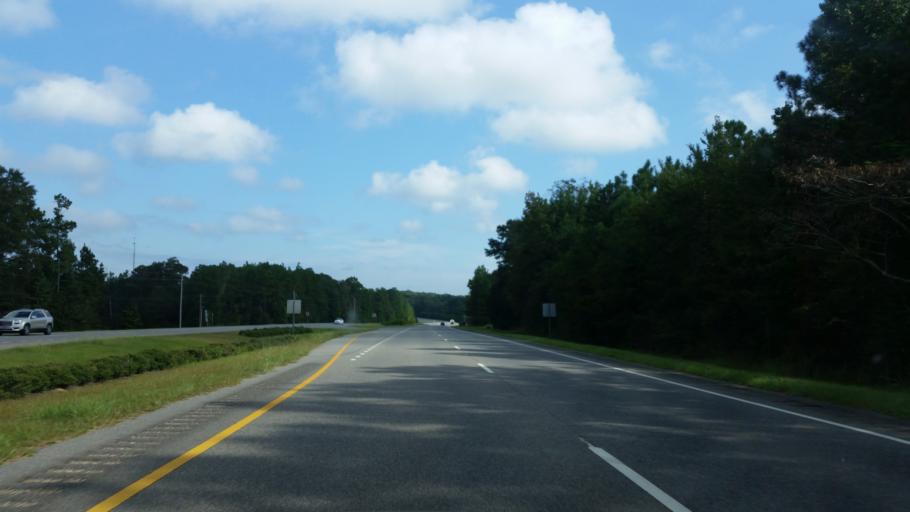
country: US
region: Alabama
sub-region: Baldwin County
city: Bay Minette
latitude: 30.9456
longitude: -87.7639
